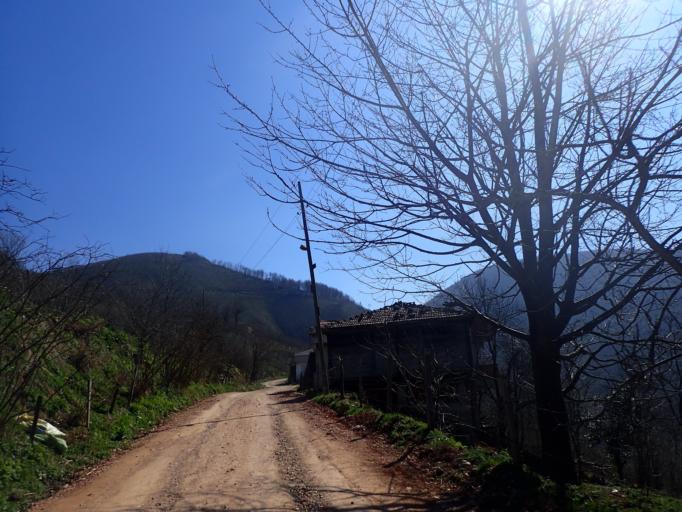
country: TR
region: Ordu
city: Catalpinar
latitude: 40.8650
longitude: 37.4944
